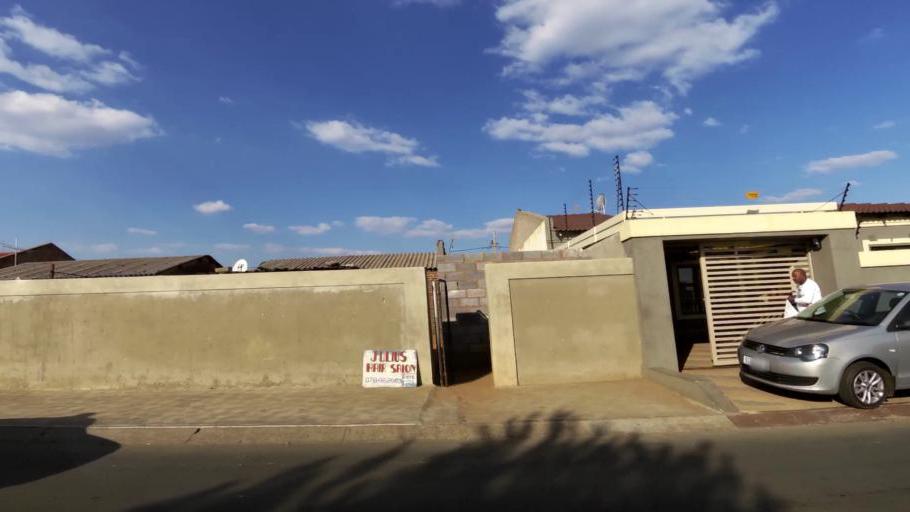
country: ZA
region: Gauteng
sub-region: City of Johannesburg Metropolitan Municipality
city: Roodepoort
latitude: -26.2112
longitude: 27.8768
